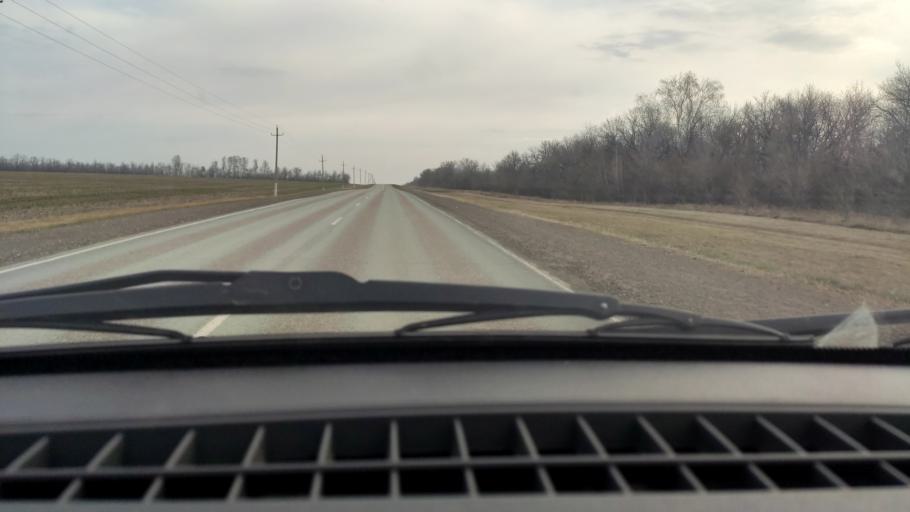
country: RU
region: Bashkortostan
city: Davlekanovo
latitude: 54.3122
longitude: 55.1461
